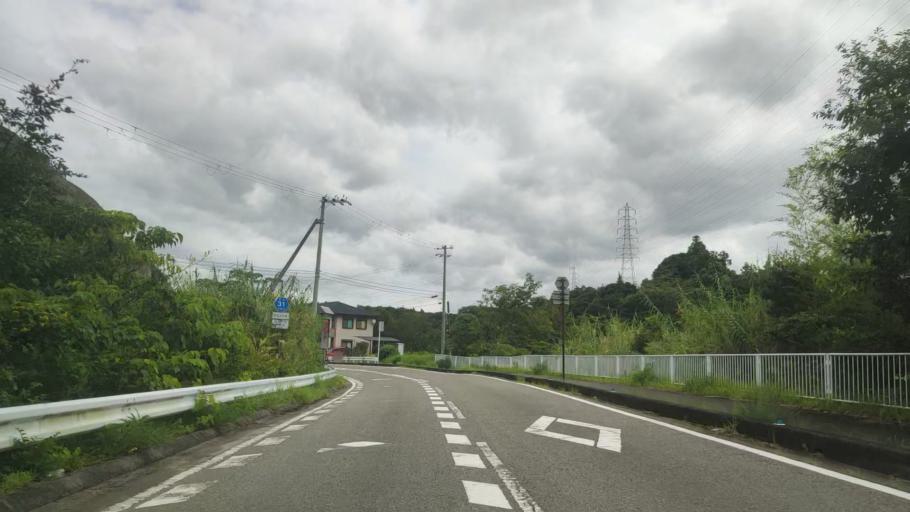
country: JP
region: Wakayama
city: Tanabe
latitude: 33.6861
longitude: 135.3884
